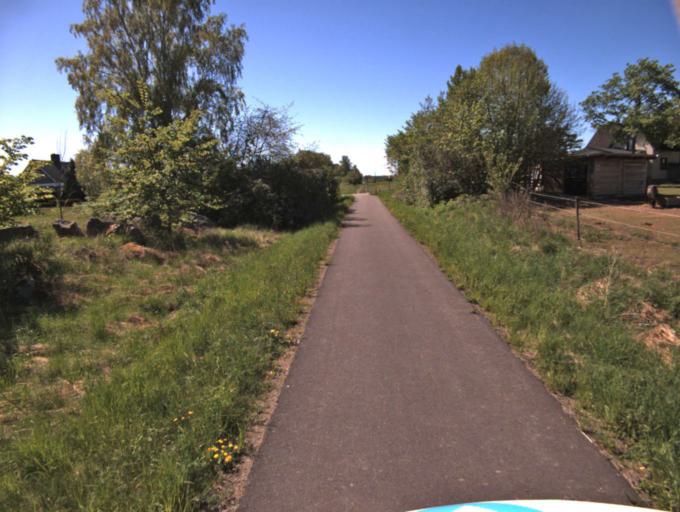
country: SE
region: Skane
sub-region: Kristianstads Kommun
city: Norra Asum
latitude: 55.9503
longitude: 14.1532
